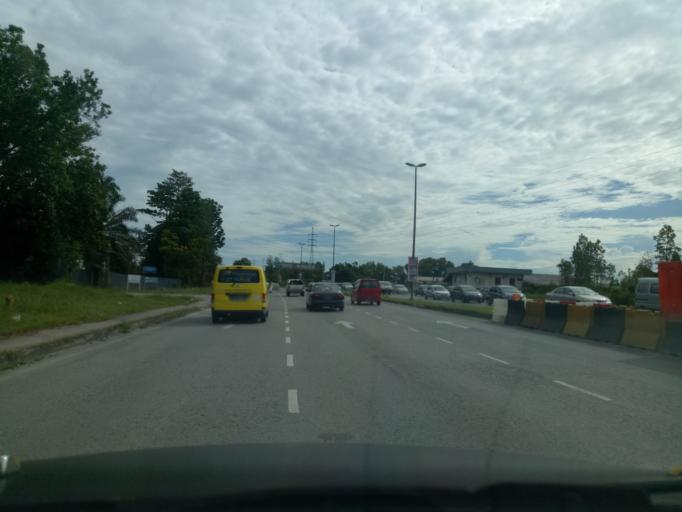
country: MY
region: Sarawak
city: Kuching
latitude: 1.4842
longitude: 110.3311
